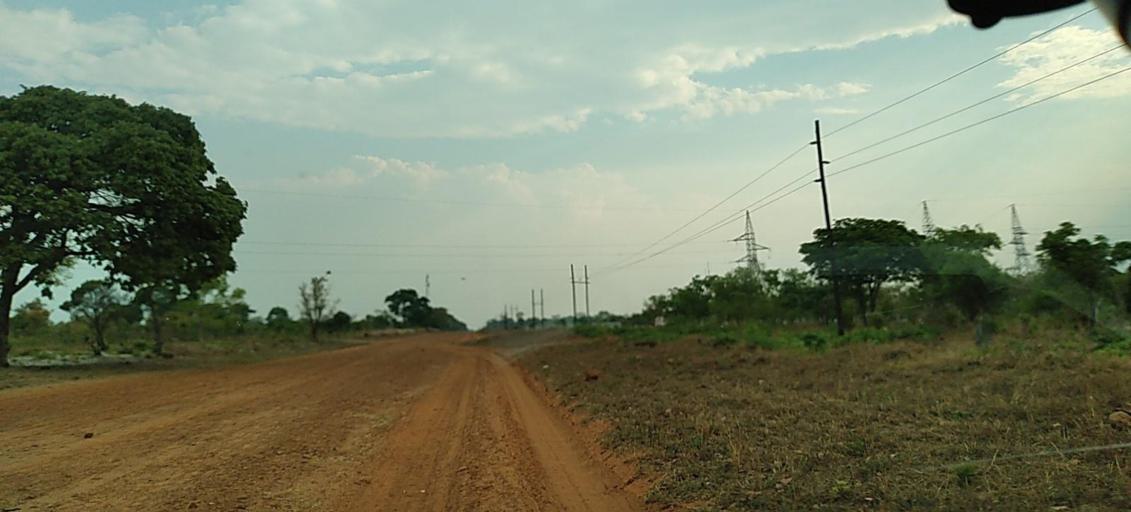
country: ZM
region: North-Western
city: Kabompo
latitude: -13.8766
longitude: 23.6656
